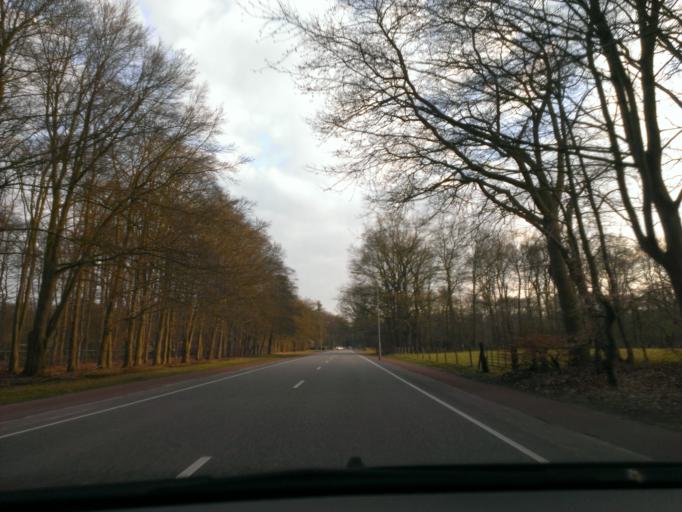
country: NL
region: Gelderland
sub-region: Gemeente Hattem
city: Hattem
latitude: 52.4559
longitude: 6.0672
